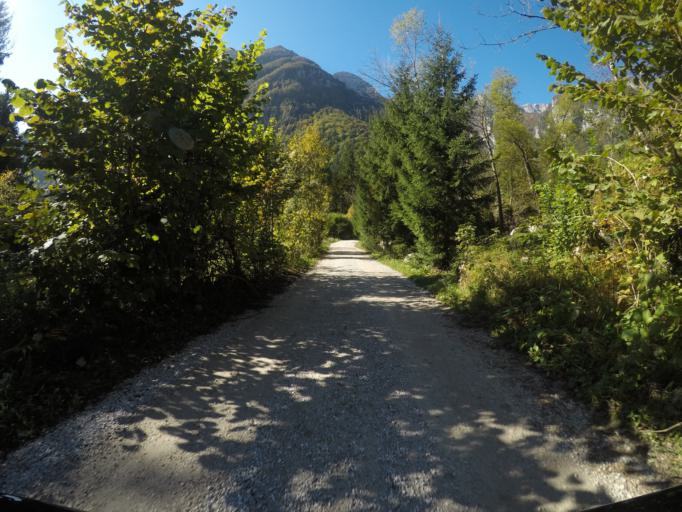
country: SI
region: Kamnik
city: Mekinje
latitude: 46.3291
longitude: 14.5862
